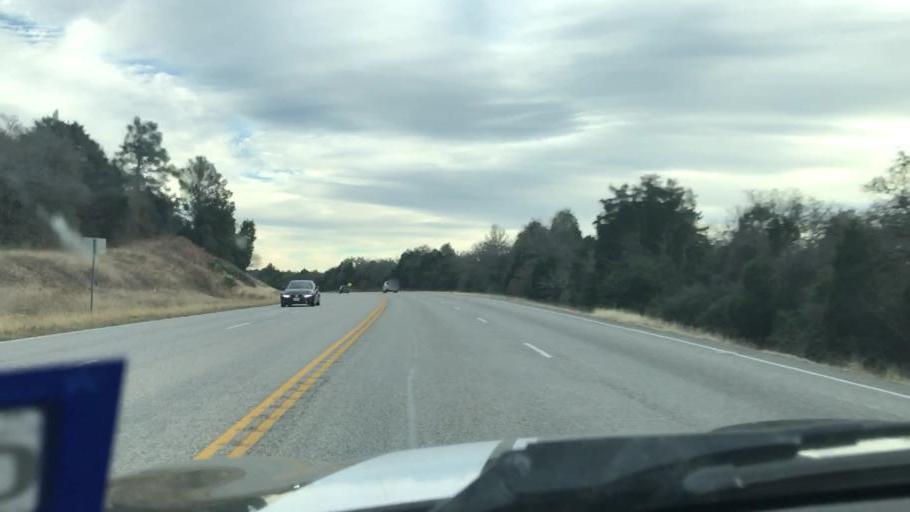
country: US
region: Texas
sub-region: Bastrop County
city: Camp Swift
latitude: 30.2499
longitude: -97.2241
